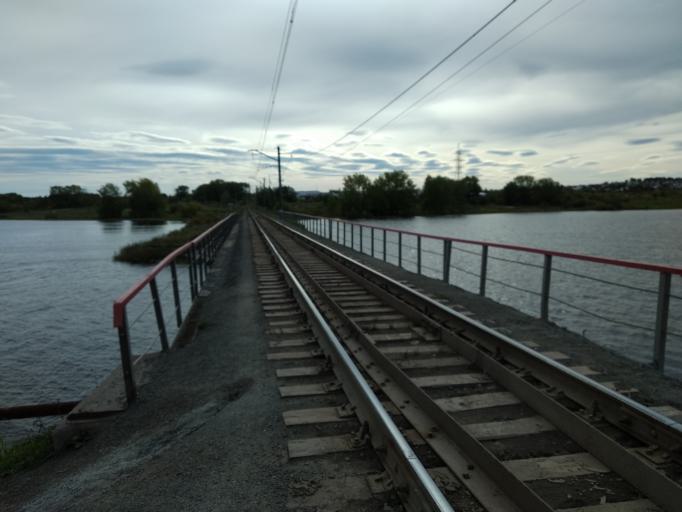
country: RU
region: Sverdlovsk
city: Krasnotur'insk
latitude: 59.7767
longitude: 60.1593
